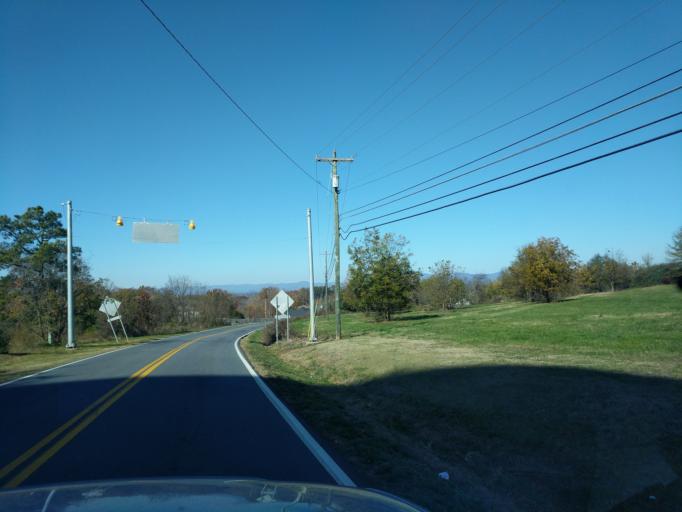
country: US
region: South Carolina
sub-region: Greenville County
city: Greer
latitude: 34.9492
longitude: -82.2641
